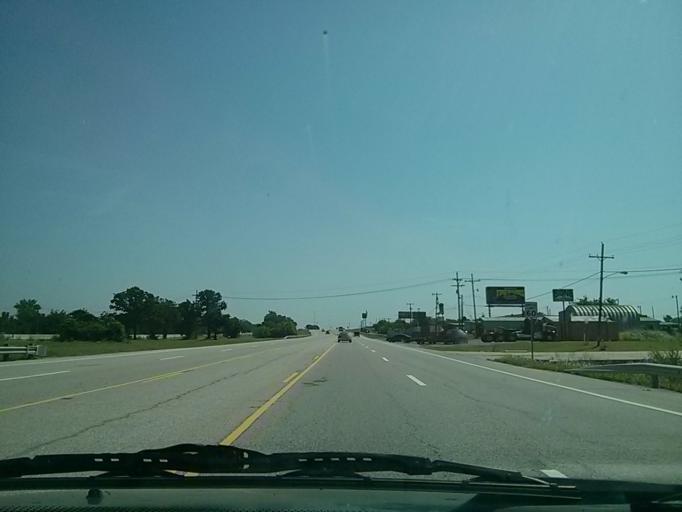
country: US
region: Oklahoma
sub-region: Tulsa County
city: Oakhurst
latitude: 36.0681
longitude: -96.0643
